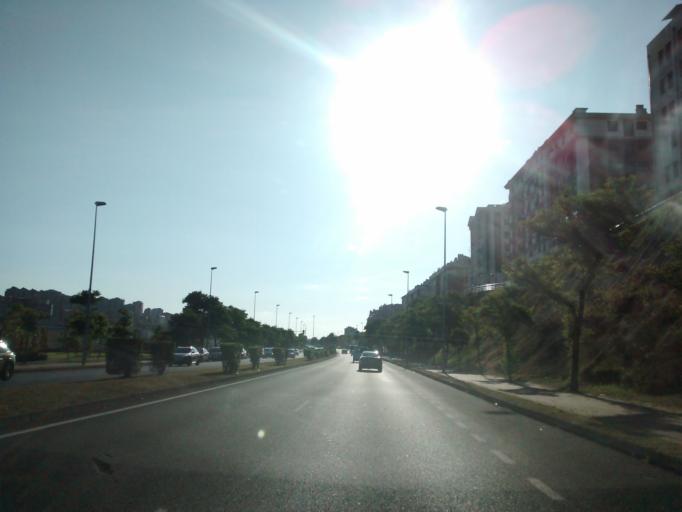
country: ES
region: Cantabria
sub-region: Provincia de Cantabria
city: Santander
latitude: 43.4755
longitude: -3.8011
